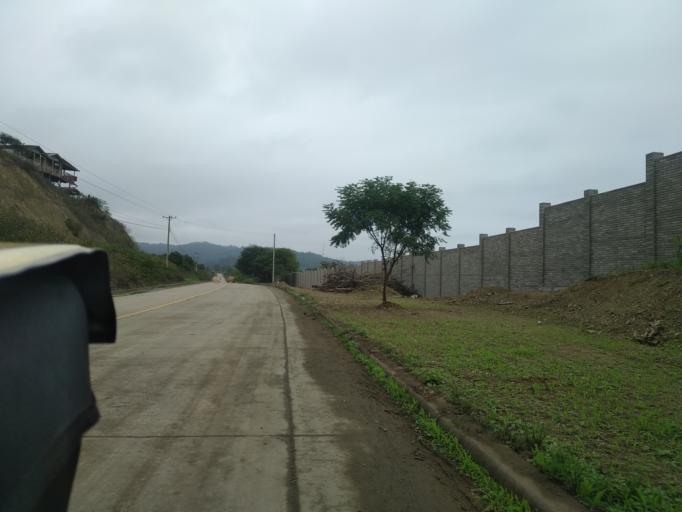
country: EC
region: Manabi
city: Jipijapa
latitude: -1.6556
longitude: -80.8201
